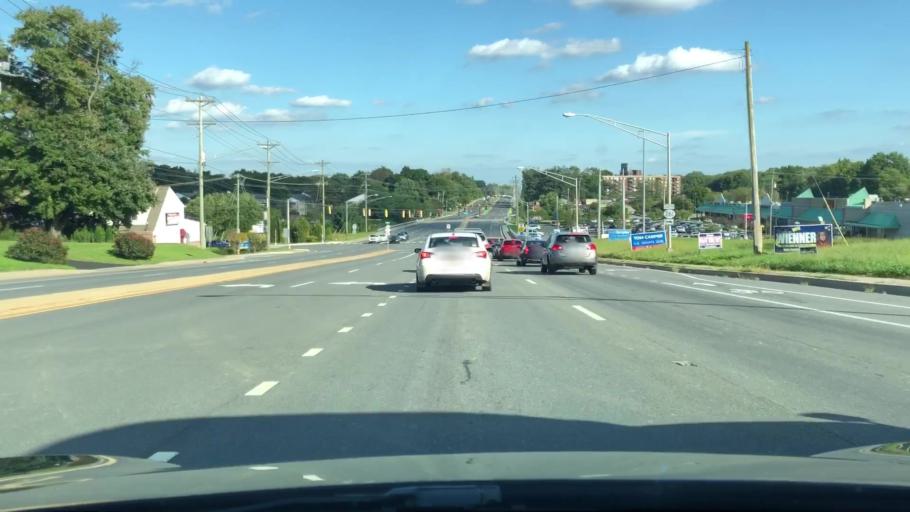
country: US
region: Delaware
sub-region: New Castle County
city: Claymont
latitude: 39.8249
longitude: -75.5025
